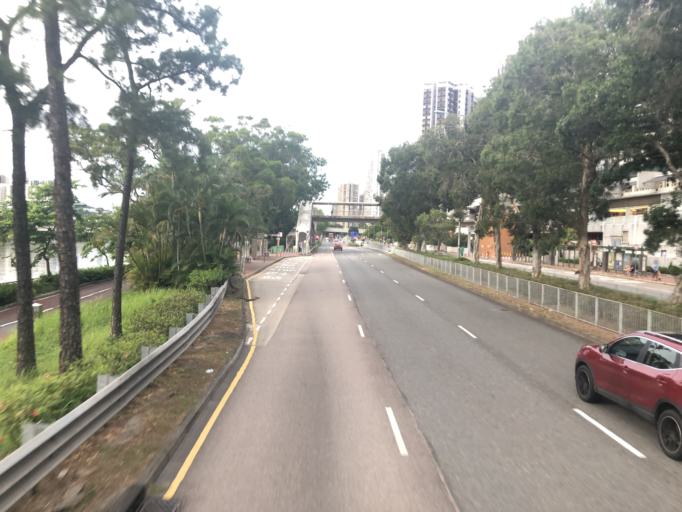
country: HK
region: Sha Tin
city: Sha Tin
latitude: 22.3845
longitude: 114.1976
